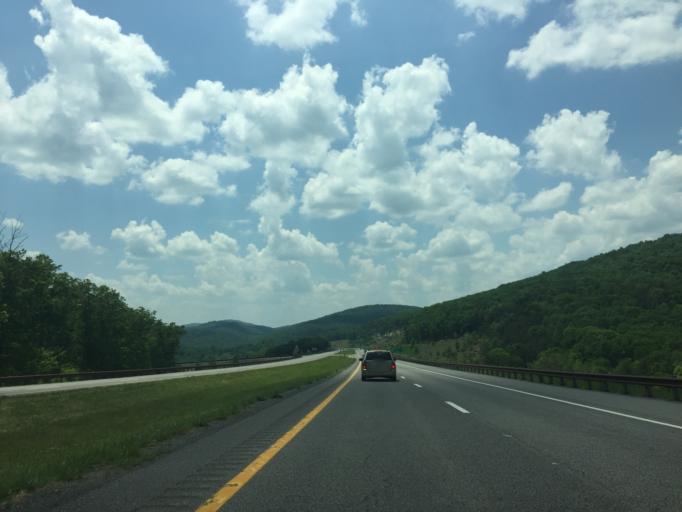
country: US
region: Virginia
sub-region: Shenandoah County
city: Woodstock
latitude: 39.0534
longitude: -78.6961
